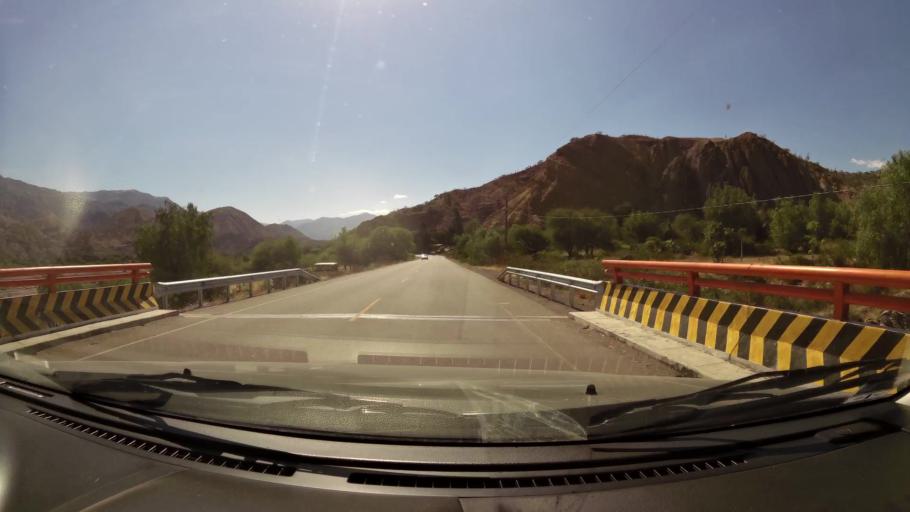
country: PE
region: Ayacucho
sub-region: Provincia de Huanta
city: Luricocha
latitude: -12.8747
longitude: -74.3227
